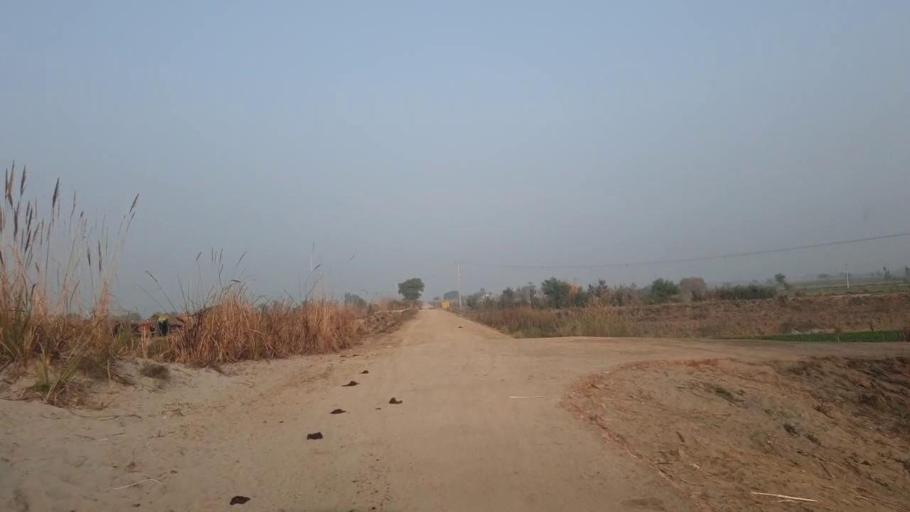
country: PK
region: Sindh
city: Shahdadpur
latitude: 25.8940
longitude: 68.6091
